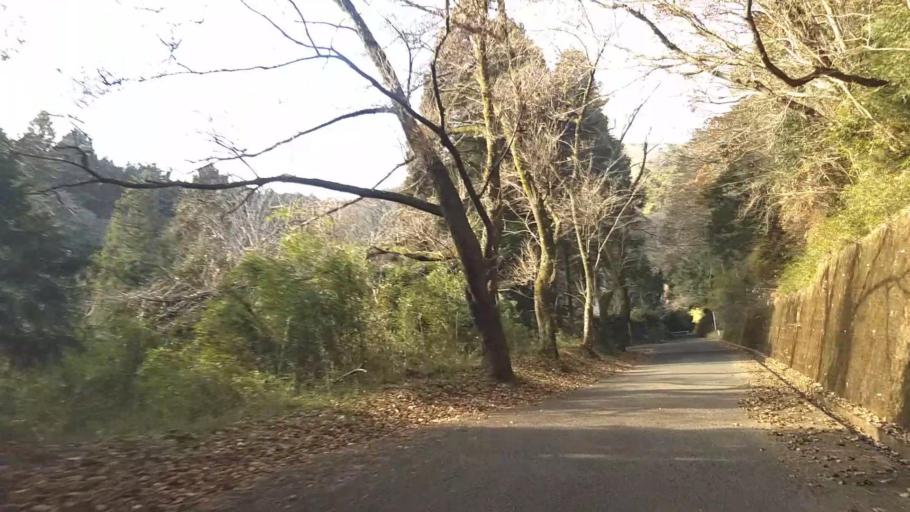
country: JP
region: Kanagawa
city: Isehara
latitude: 35.4449
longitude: 139.2848
